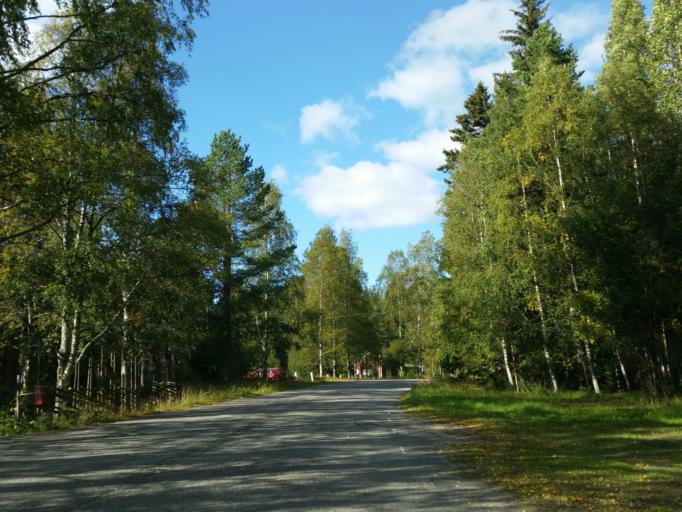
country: SE
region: Vaesterbotten
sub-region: Robertsfors Kommun
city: Robertsfors
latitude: 64.0486
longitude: 20.8505
